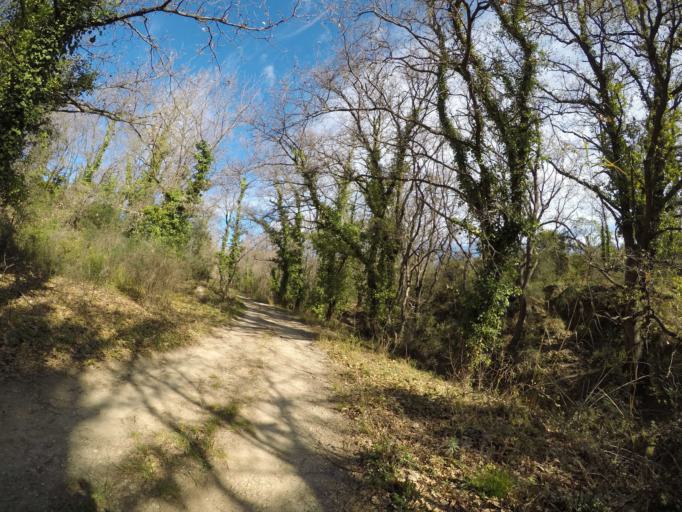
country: FR
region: Languedoc-Roussillon
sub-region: Departement des Pyrenees-Orientales
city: Millas
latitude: 42.7100
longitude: 2.6994
